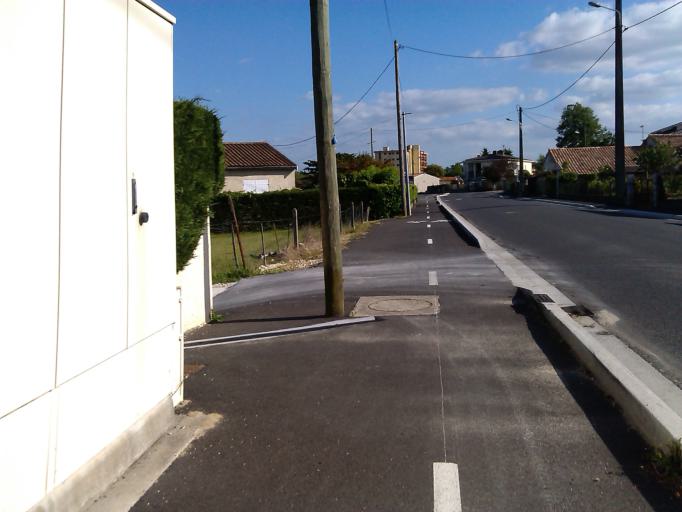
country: FR
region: Aquitaine
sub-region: Departement de la Gironde
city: Saint-Gervais
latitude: 45.0008
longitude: -0.4475
